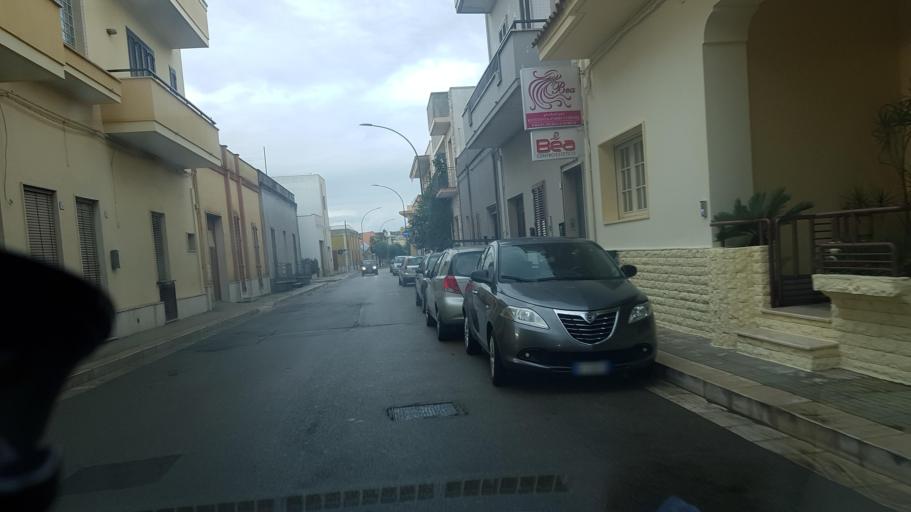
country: IT
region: Apulia
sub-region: Provincia di Lecce
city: Guagnano
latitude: 40.3985
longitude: 17.9531
